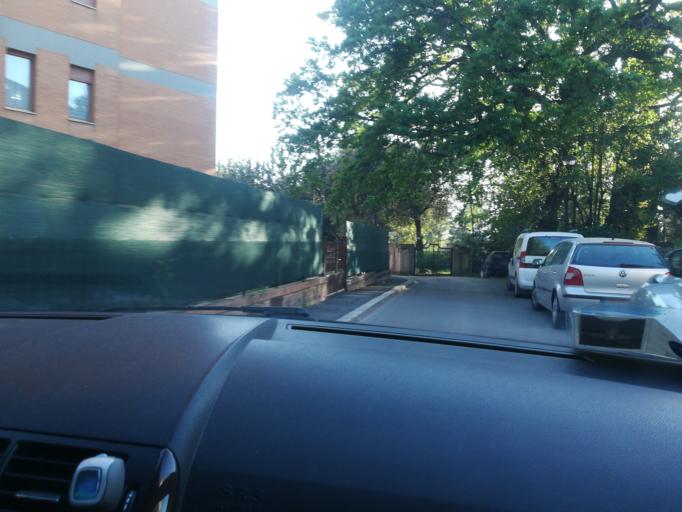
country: IT
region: The Marches
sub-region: Provincia di Macerata
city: Macerata
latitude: 43.2944
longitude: 13.4330
